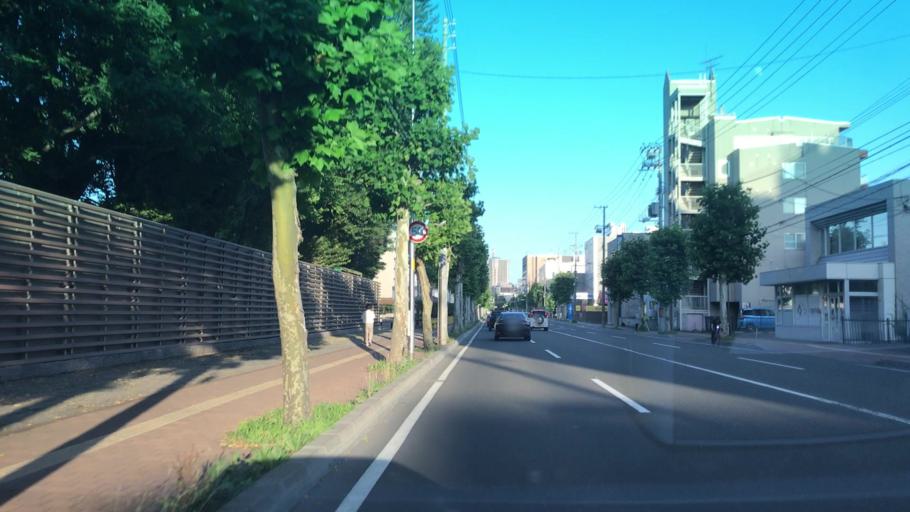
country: JP
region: Hokkaido
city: Sapporo
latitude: 43.0745
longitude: 141.3253
